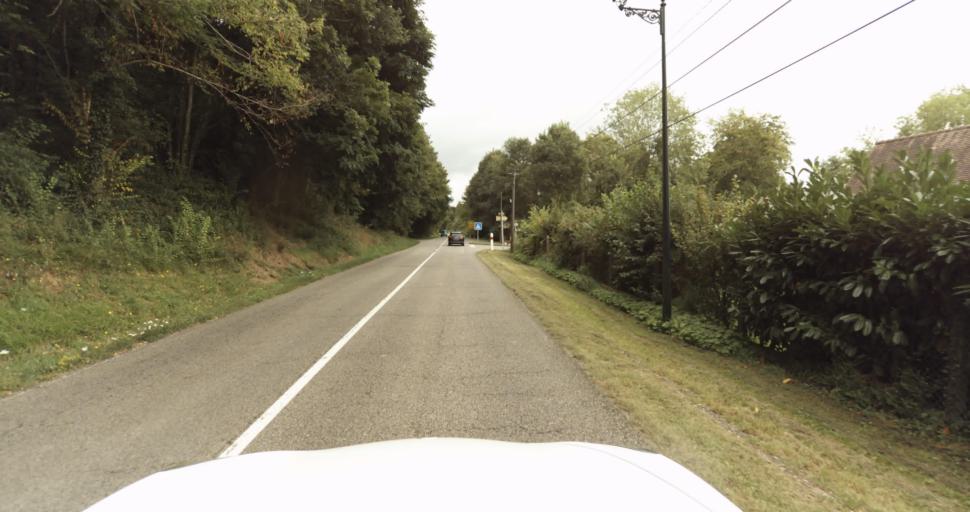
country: FR
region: Haute-Normandie
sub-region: Departement de l'Eure
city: Saint-Sebastien-de-Morsent
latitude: 48.9990
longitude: 1.0620
